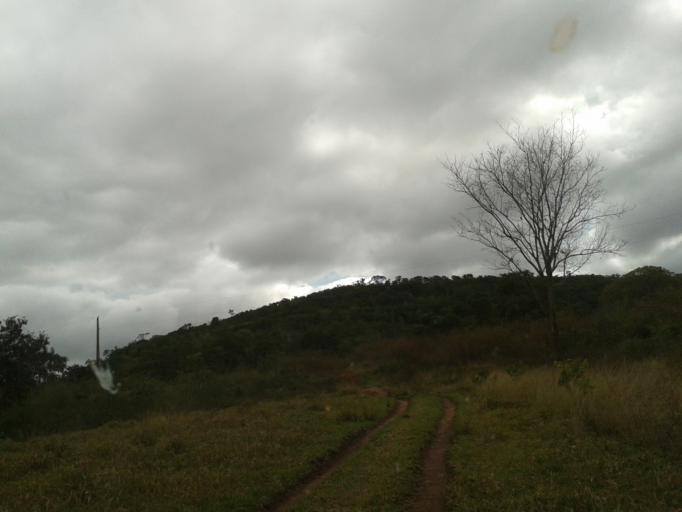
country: BR
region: Minas Gerais
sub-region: Campina Verde
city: Campina Verde
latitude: -19.4622
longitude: -49.5896
